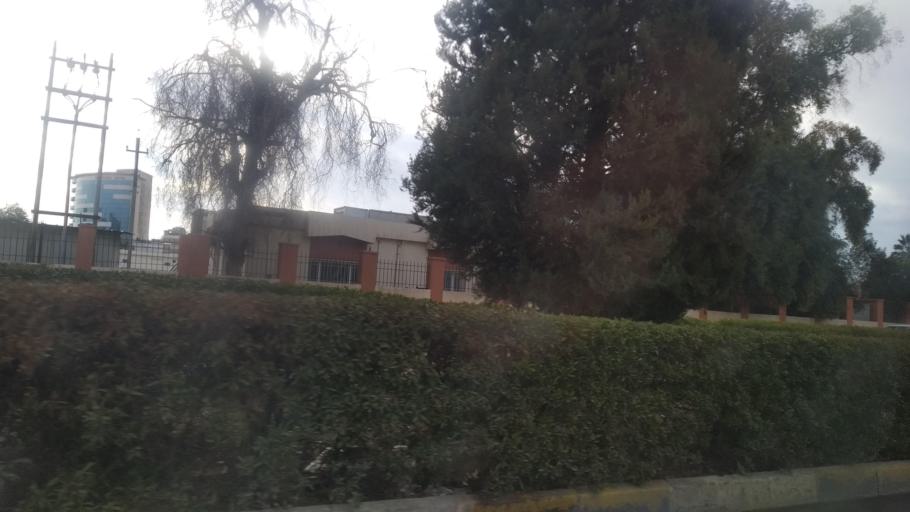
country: IQ
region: Arbil
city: Erbil
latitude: 36.2003
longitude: 44.0196
